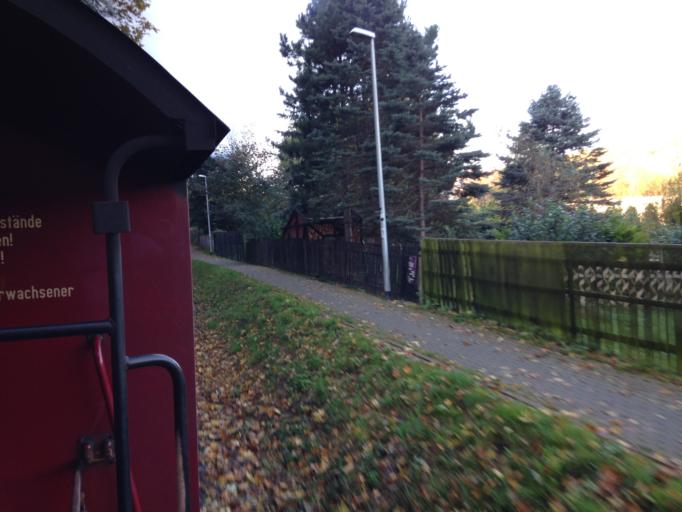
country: DE
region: Saxony-Anhalt
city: Wernigerode
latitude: 51.8285
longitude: 10.7747
